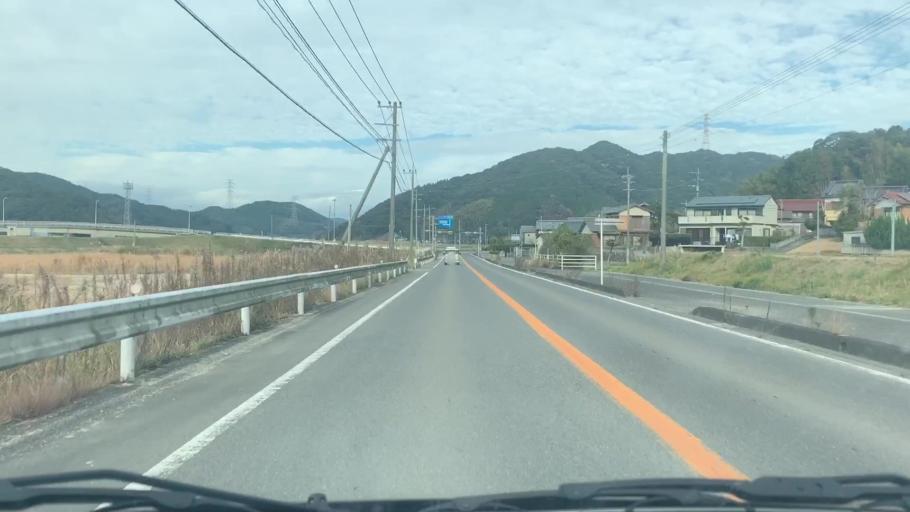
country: JP
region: Saga Prefecture
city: Karatsu
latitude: 33.3731
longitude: 130.0020
